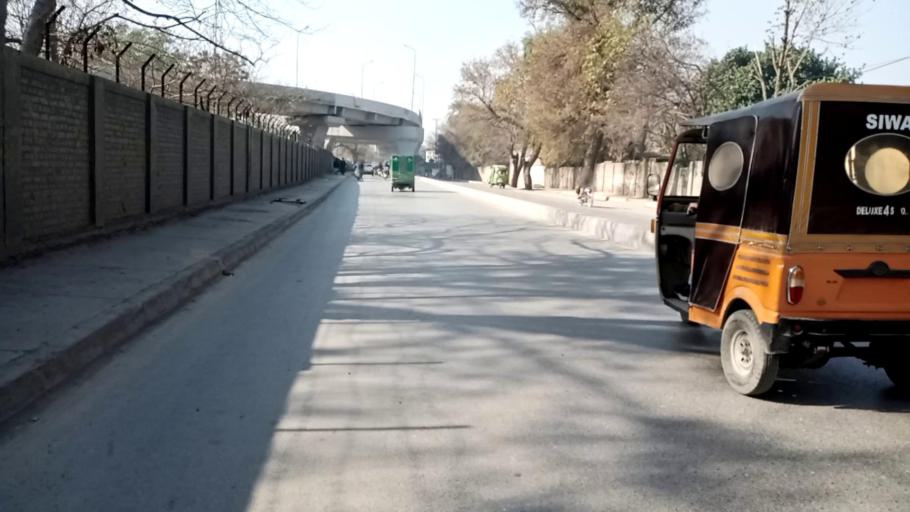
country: PK
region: Khyber Pakhtunkhwa
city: Peshawar
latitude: 34.0047
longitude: 71.5531
